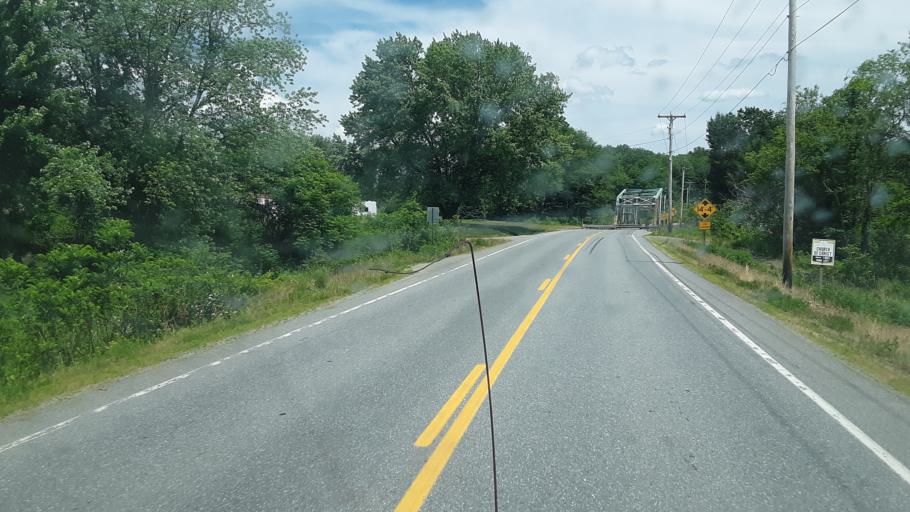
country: US
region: Maine
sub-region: Franklin County
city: Chesterville
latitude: 44.6158
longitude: -70.0845
